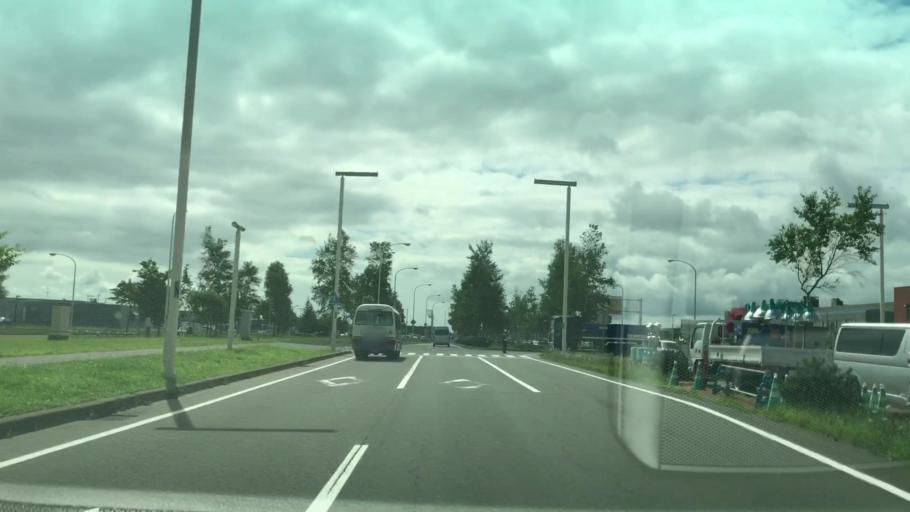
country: JP
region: Hokkaido
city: Chitose
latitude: 42.7839
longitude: 141.6775
